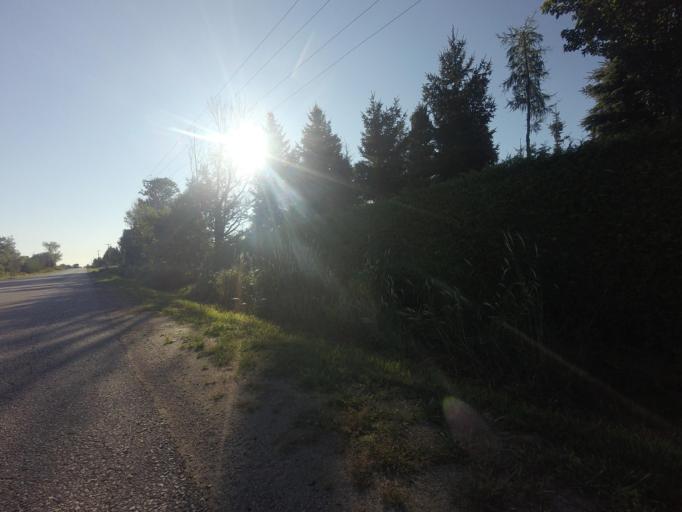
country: CA
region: Ontario
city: Bradford West Gwillimbury
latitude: 44.0532
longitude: -79.7227
